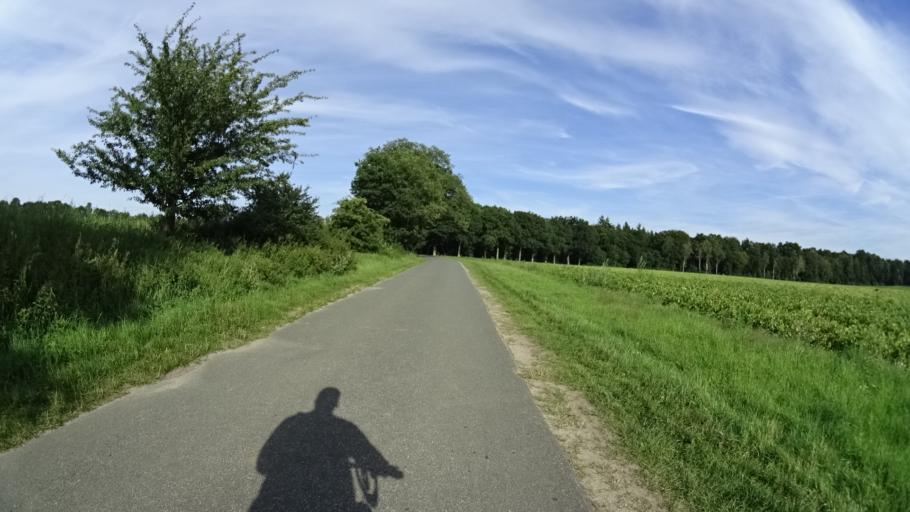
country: DE
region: Lower Saxony
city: Reppenstedt
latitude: 53.2369
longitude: 10.3645
